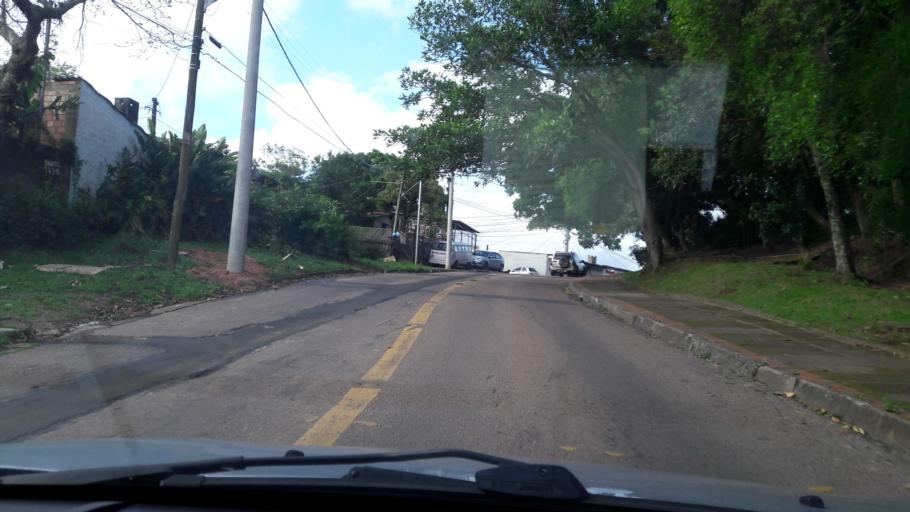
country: BR
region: Rio Grande do Sul
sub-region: Porto Alegre
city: Porto Alegre
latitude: -30.0850
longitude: -51.1998
